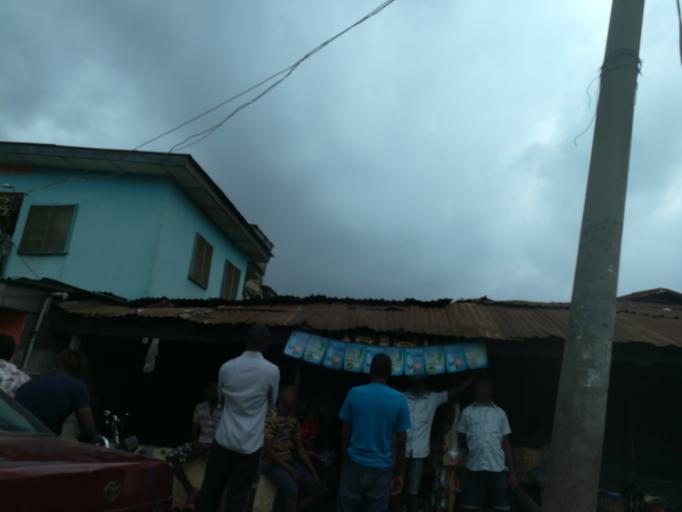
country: NG
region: Lagos
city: Oshodi
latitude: 6.5521
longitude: 3.3342
